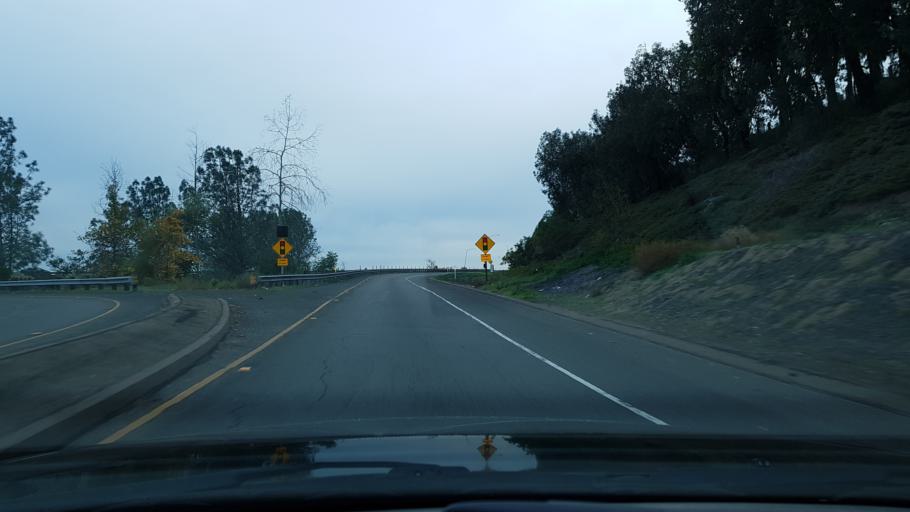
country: US
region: California
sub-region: San Diego County
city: Fairbanks Ranch
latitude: 32.9592
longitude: -117.1159
